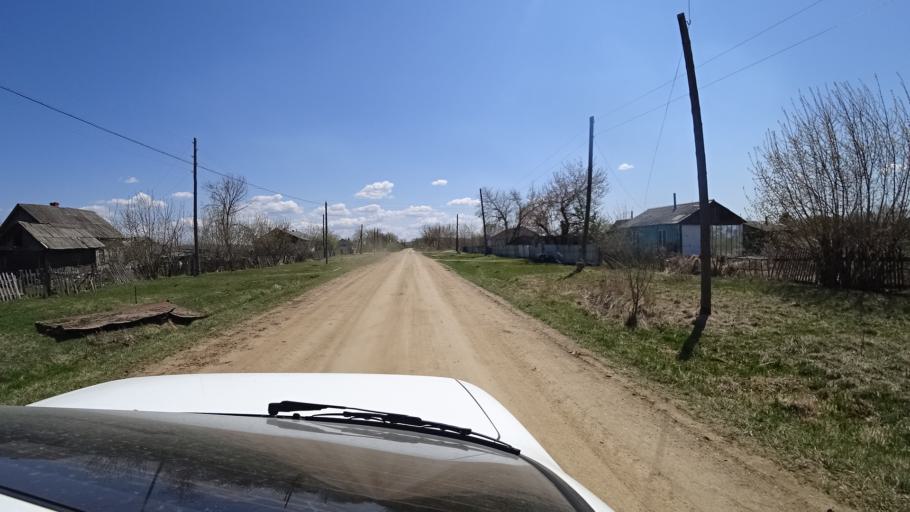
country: RU
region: Primorskiy
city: Dal'nerechensk
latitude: 45.8020
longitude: 133.7651
